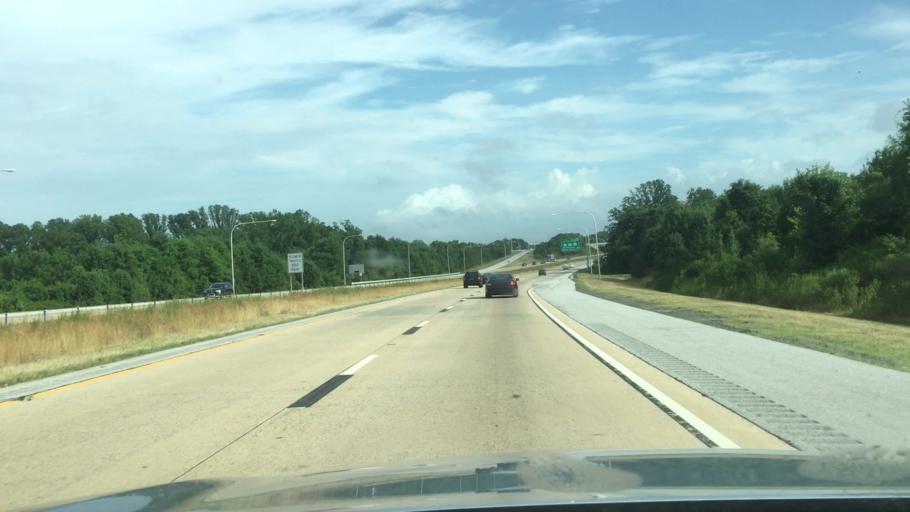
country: US
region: Delaware
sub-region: New Castle County
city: Middletown
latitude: 39.5074
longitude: -75.6475
